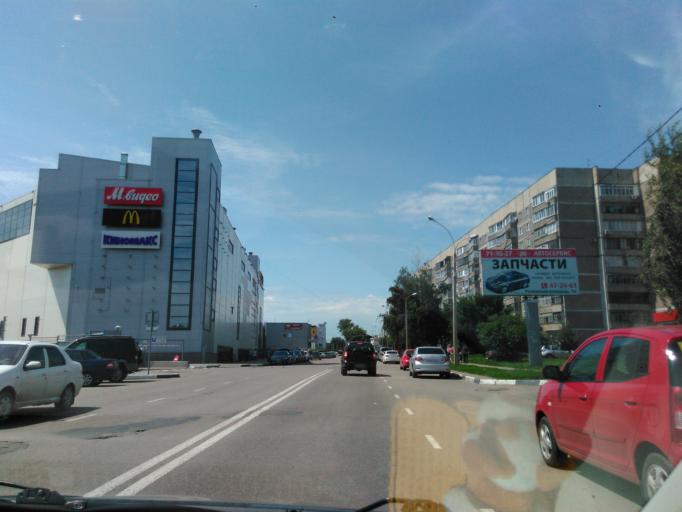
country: RU
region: Tambov
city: Tambov
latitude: 52.7288
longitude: 41.4467
